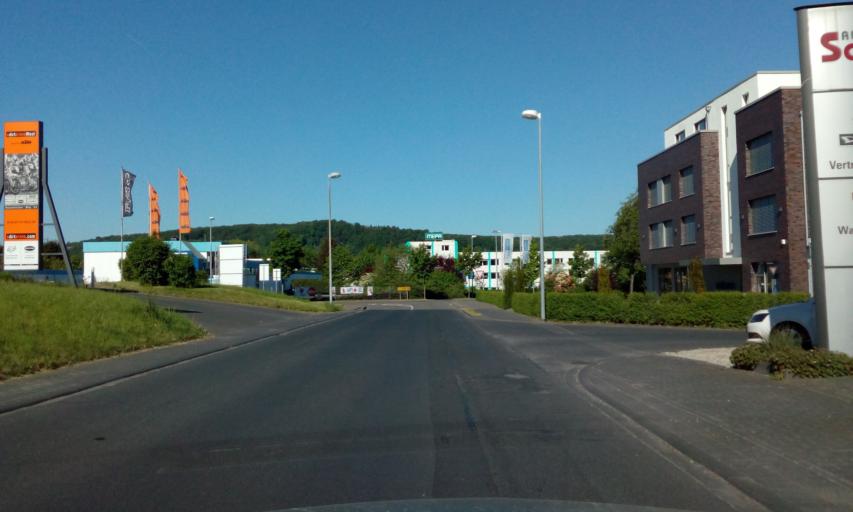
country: DE
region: Rheinland-Pfalz
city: Rheinbreitbach
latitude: 50.6243
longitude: 7.2265
